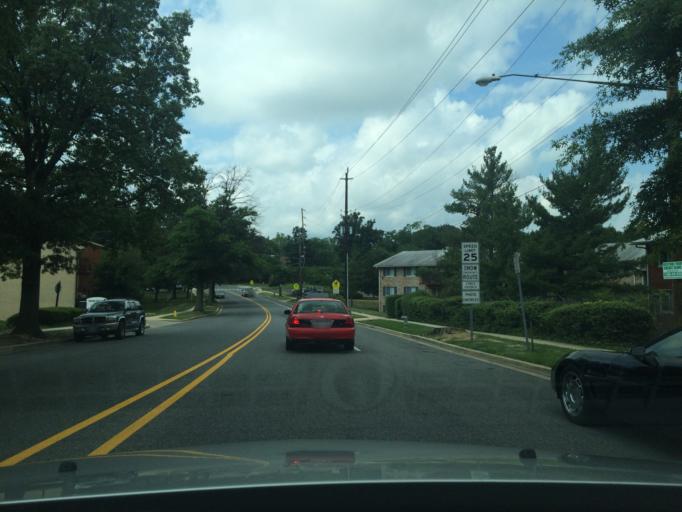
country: US
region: Maryland
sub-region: Prince George's County
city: Coral Hills
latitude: 38.8599
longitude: -76.9192
